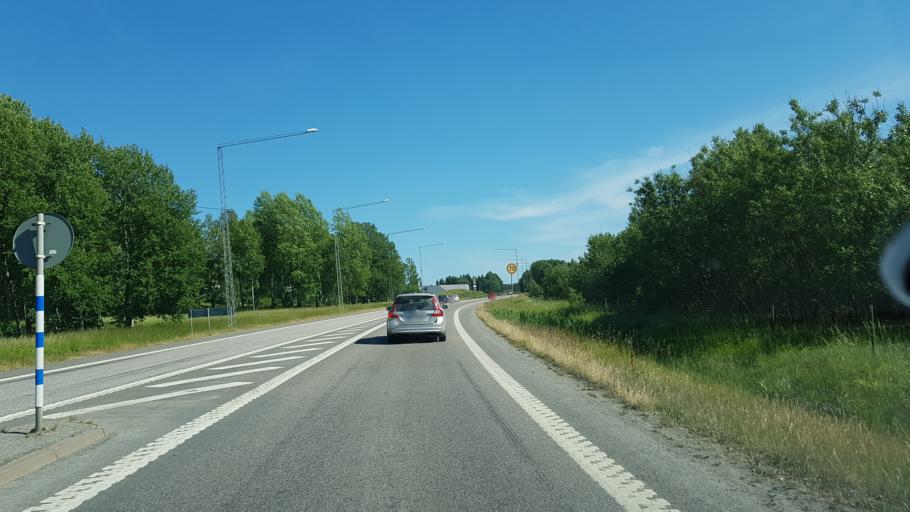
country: SE
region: Stockholm
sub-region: Sigtuna Kommun
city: Rosersberg
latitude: 59.6115
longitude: 17.8859
